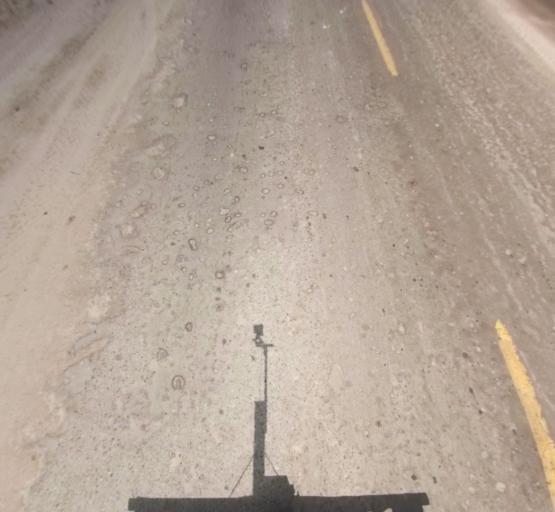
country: US
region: California
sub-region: Fresno County
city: Kerman
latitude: 36.8312
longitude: -120.2114
